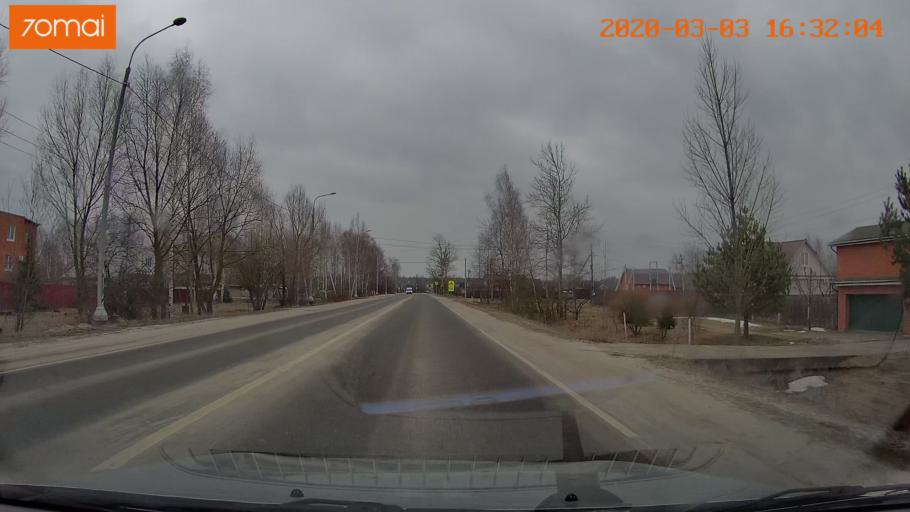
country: RU
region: Moskovskaya
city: Konobeyevo
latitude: 55.4225
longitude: 38.7304
